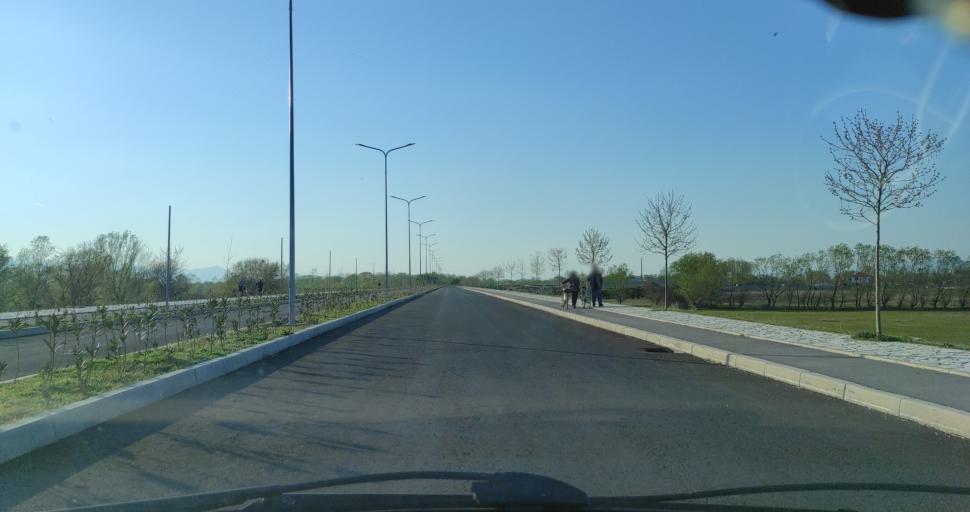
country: AL
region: Shkoder
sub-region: Rrethi i Shkodres
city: Shkoder
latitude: 42.0619
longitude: 19.4943
